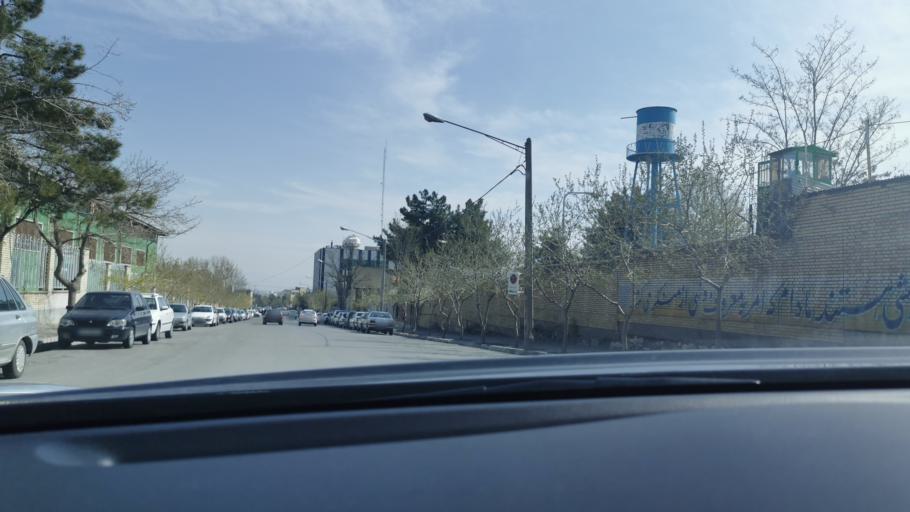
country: IR
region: Razavi Khorasan
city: Mashhad
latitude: 36.2804
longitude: 59.5493
